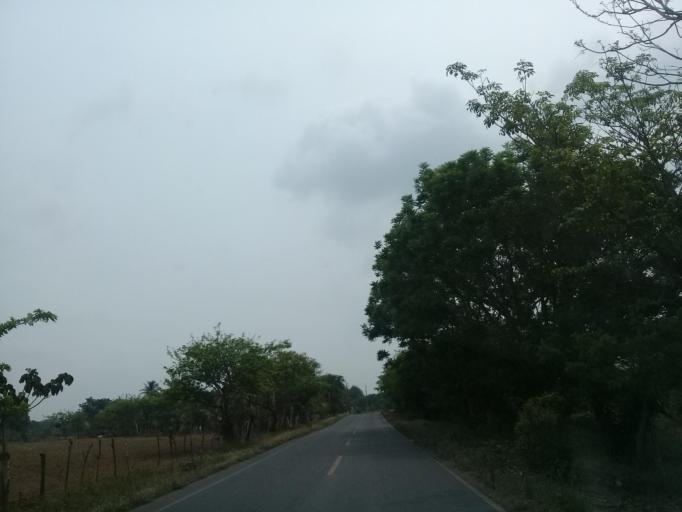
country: MX
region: Veracruz
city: Jamapa
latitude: 19.0514
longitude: -96.2056
